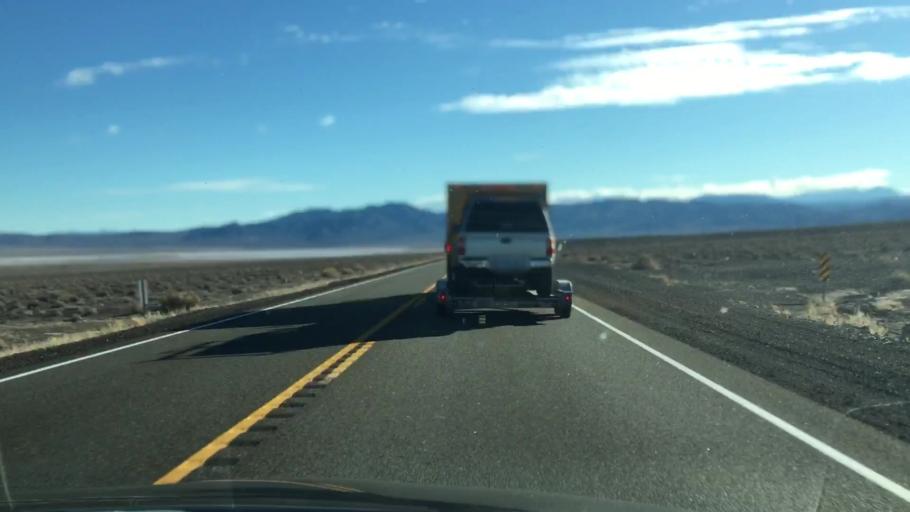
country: US
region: Nevada
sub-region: Mineral County
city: Hawthorne
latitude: 38.3361
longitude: -118.1031
